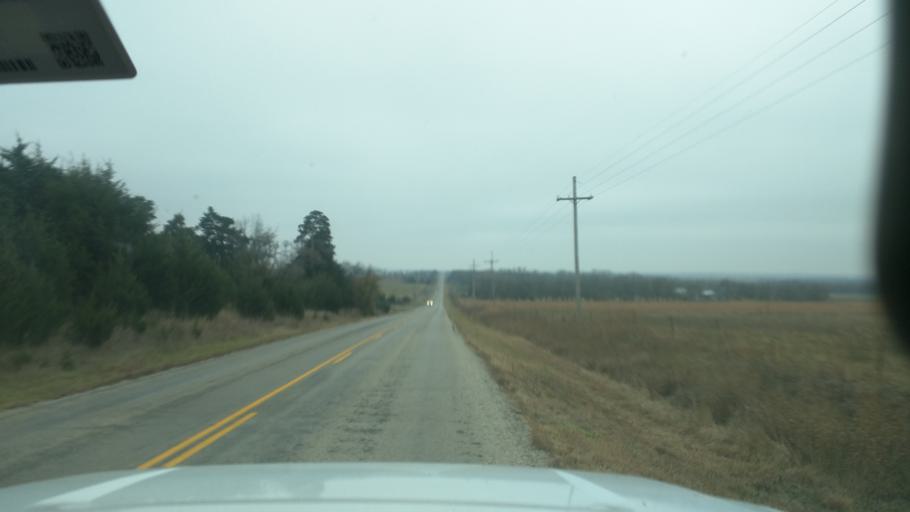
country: US
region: Kansas
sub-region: Lyon County
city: Emporia
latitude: 38.5666
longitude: -96.2611
